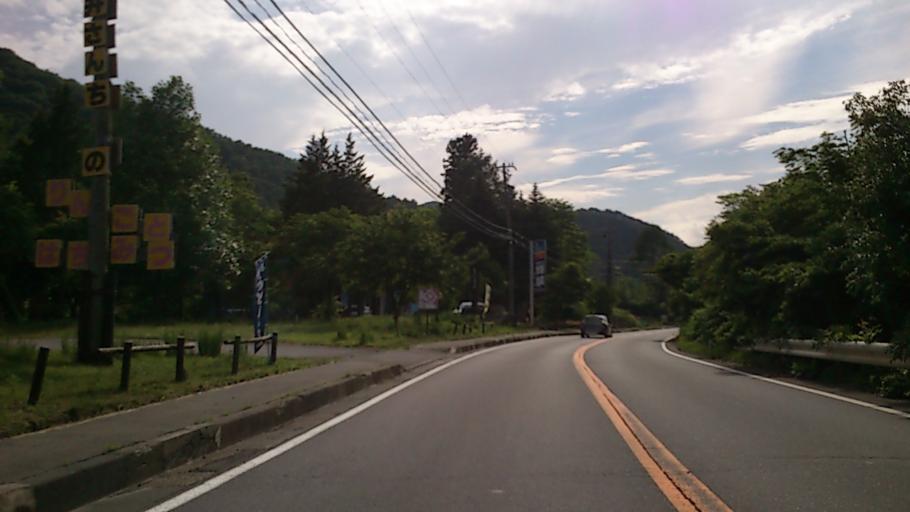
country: JP
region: Nagano
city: Saku
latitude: 36.2182
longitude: 138.5702
